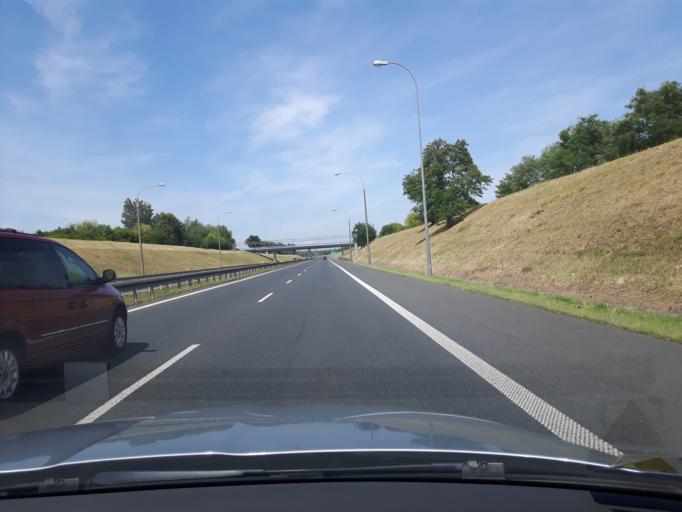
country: PL
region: Masovian Voivodeship
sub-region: Powiat nowodworski
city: Zakroczym
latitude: 52.4321
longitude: 20.6519
